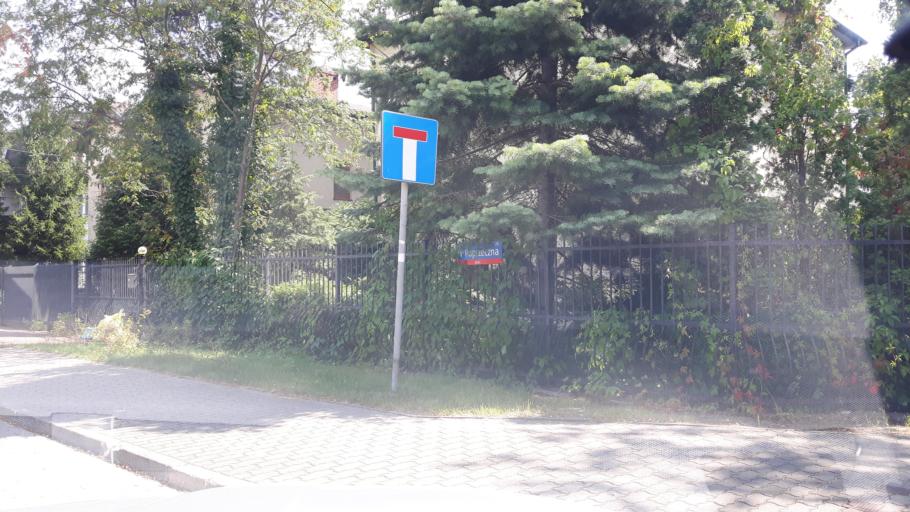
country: PL
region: Masovian Voivodeship
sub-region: Warszawa
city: Wawer
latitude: 52.2211
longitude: 21.1612
